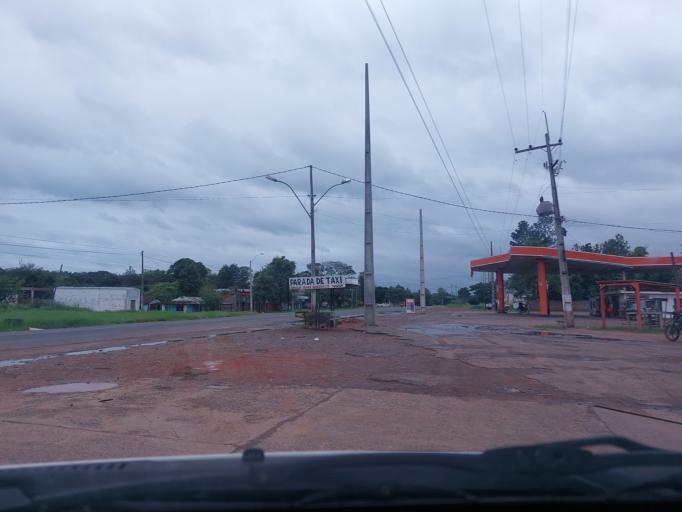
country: PY
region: San Pedro
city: Guayaybi
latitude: -24.6782
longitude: -56.4003
